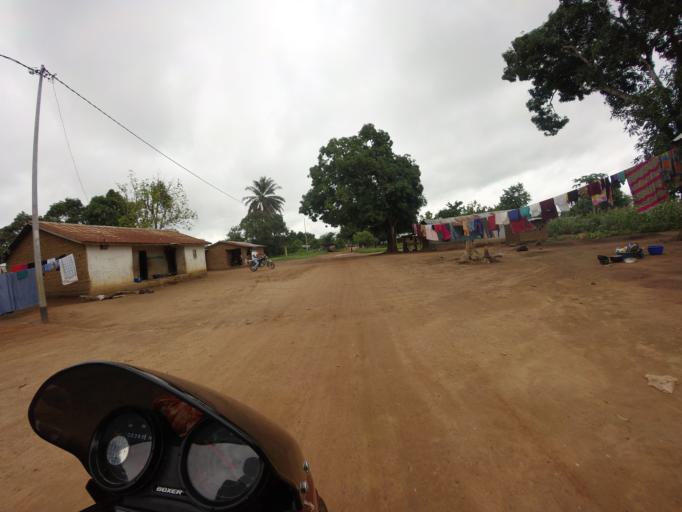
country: SL
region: Eastern Province
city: Koidu
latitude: 8.6438
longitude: -10.9250
